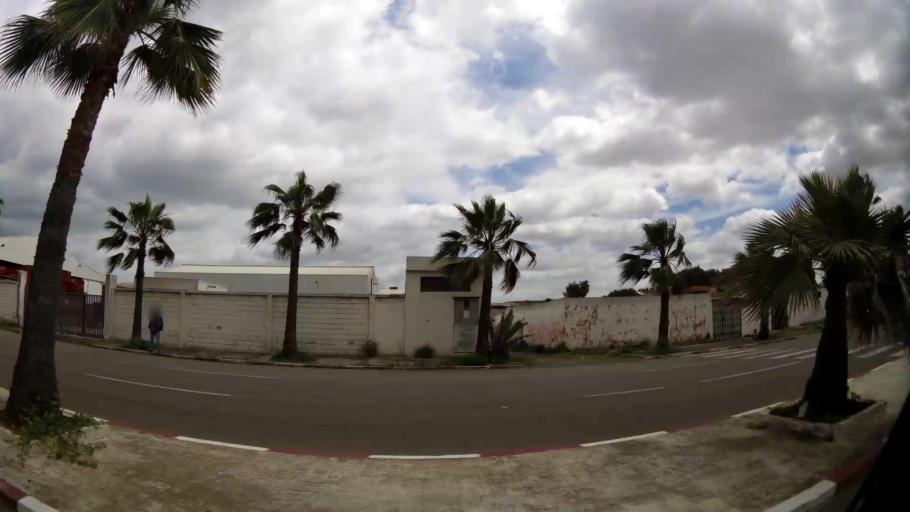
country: MA
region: Grand Casablanca
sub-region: Casablanca
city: Casablanca
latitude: 33.6134
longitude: -7.5510
